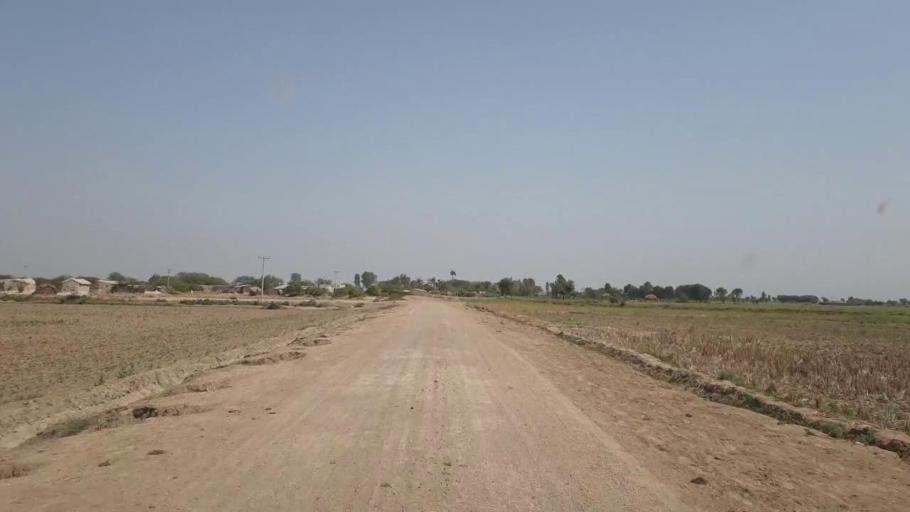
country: PK
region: Sindh
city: Jati
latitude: 24.4862
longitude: 68.5554
